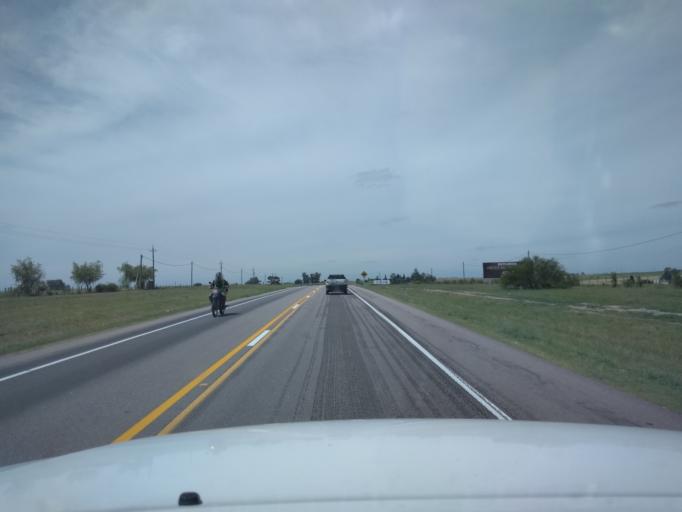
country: UY
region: Florida
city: Florida
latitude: -34.1773
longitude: -56.1907
